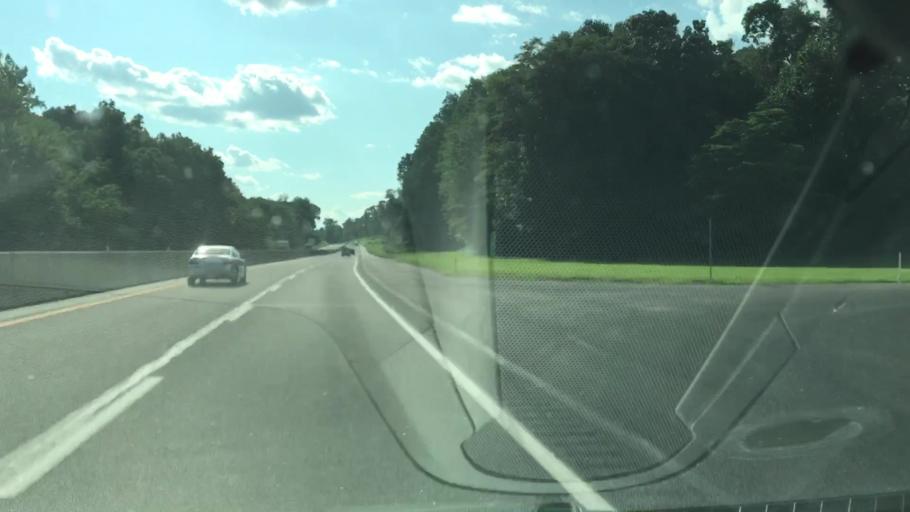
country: US
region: Pennsylvania
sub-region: Lebanon County
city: Cornwall
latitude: 40.2285
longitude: -76.4542
